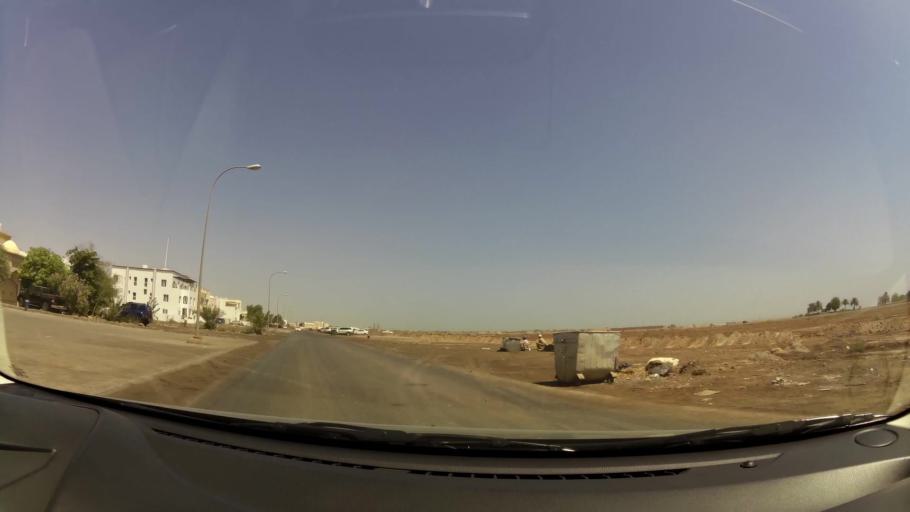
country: OM
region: Muhafazat Masqat
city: As Sib al Jadidah
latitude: 23.6242
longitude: 58.2593
